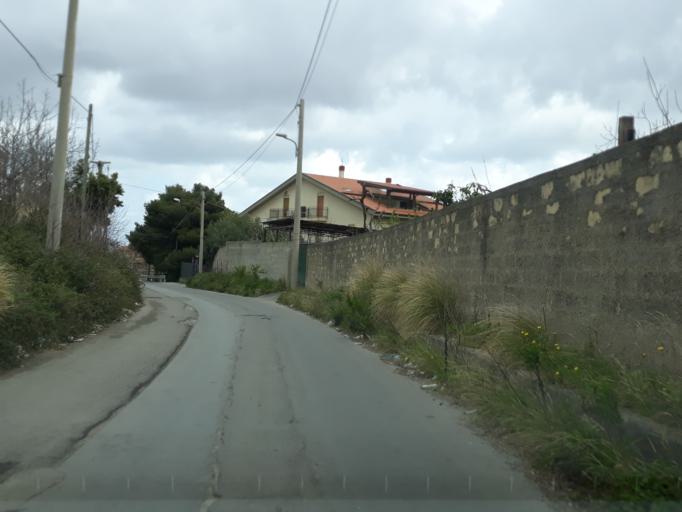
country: IT
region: Sicily
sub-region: Palermo
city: Monreale
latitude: 38.0809
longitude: 13.2963
